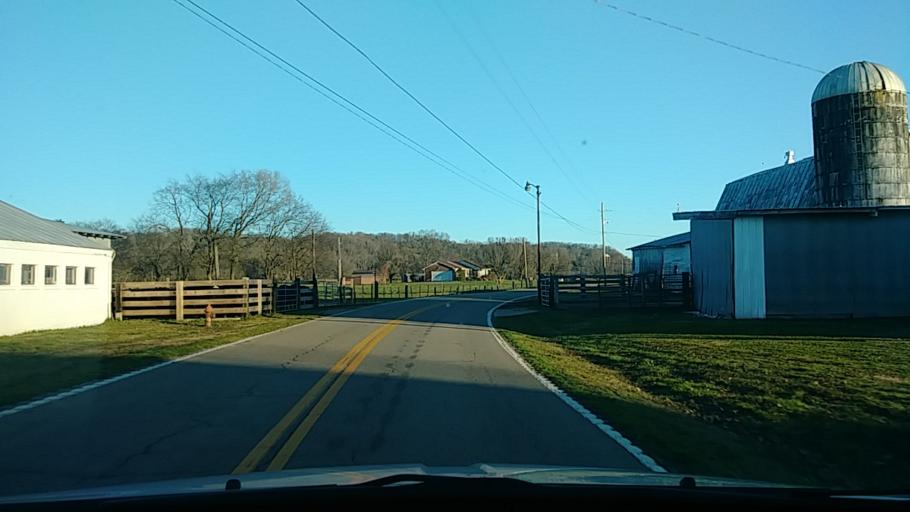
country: US
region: Tennessee
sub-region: Jefferson County
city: White Pine
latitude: 36.1366
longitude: -83.1359
